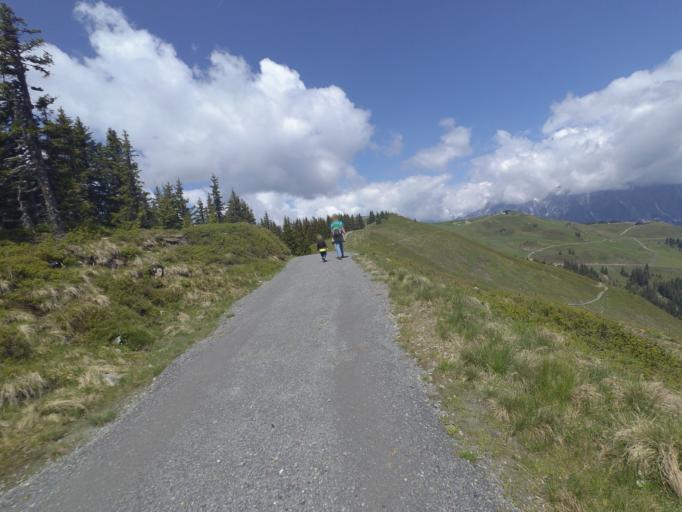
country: AT
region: Salzburg
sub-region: Politischer Bezirk Zell am See
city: Viehhofen
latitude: 47.3944
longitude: 12.7081
